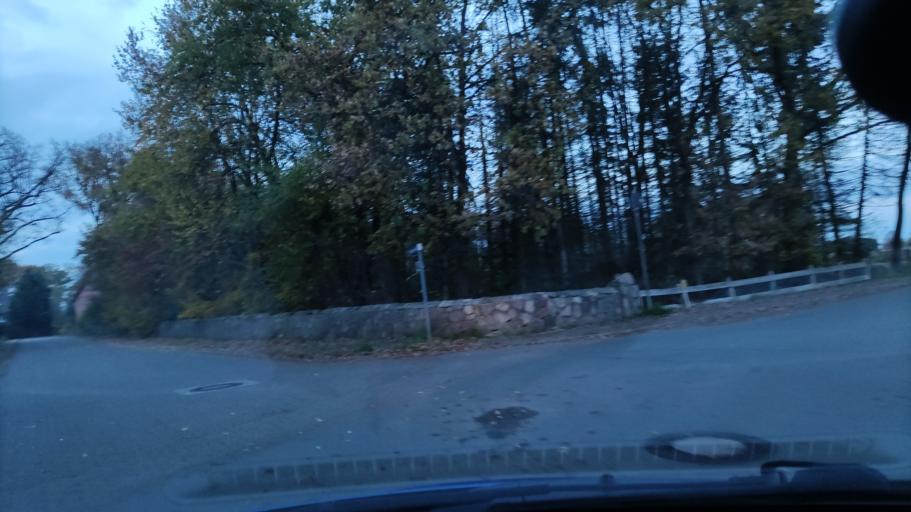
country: DE
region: Lower Saxony
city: Egestorf
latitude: 53.1406
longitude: 10.0294
